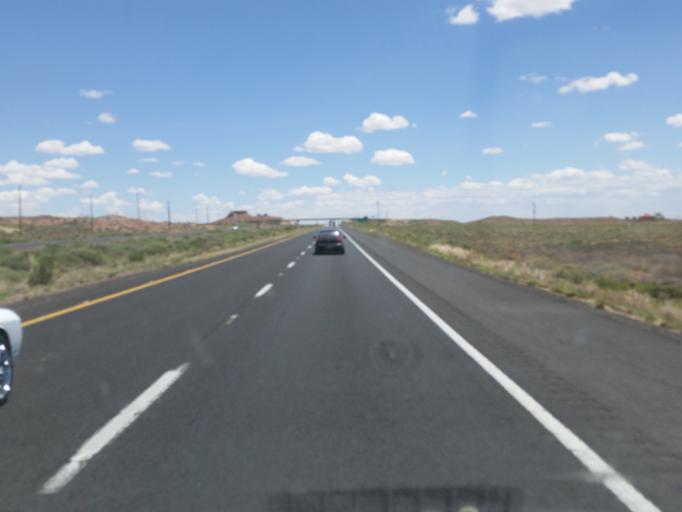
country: US
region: Arizona
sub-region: Navajo County
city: Joseph City
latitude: 34.9274
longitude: -110.2674
